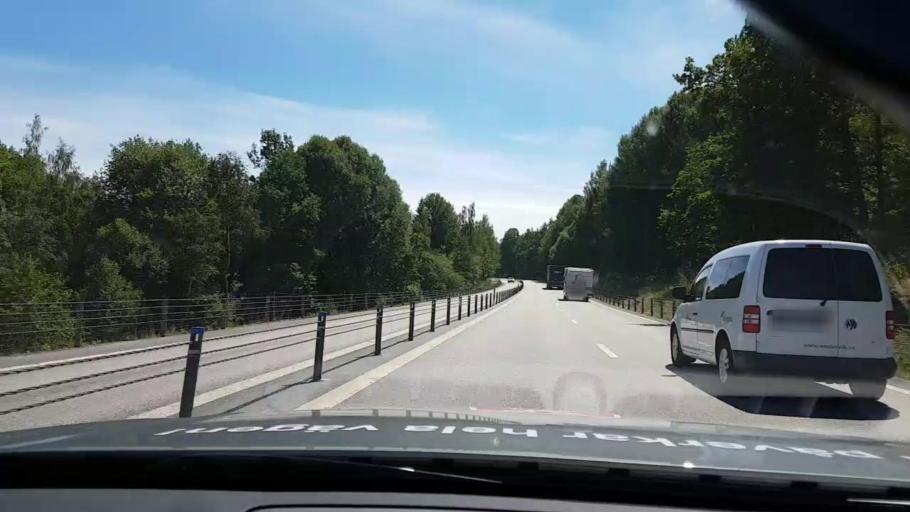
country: SE
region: Kalmar
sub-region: Vasterviks Kommun
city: Gamleby
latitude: 57.8468
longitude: 16.4360
